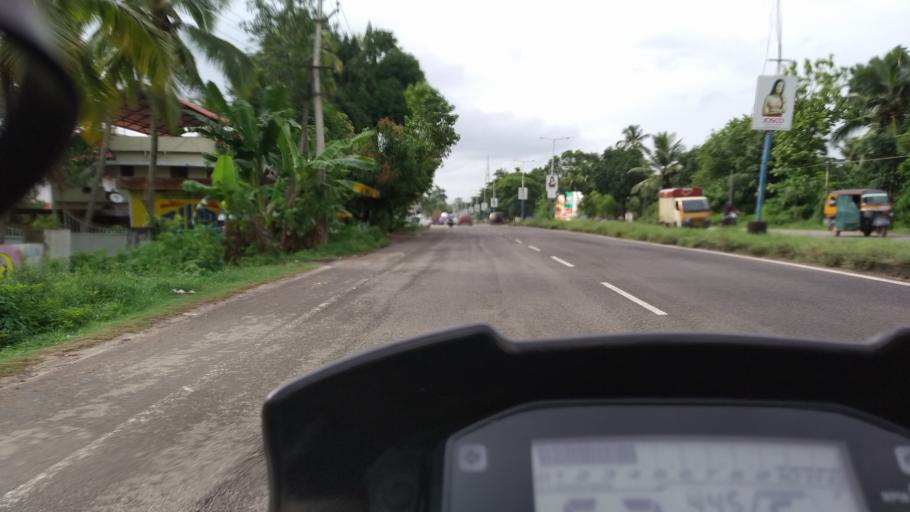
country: IN
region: Kerala
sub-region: Alappuzha
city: Kutiatodu
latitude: 9.7802
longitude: 76.3182
